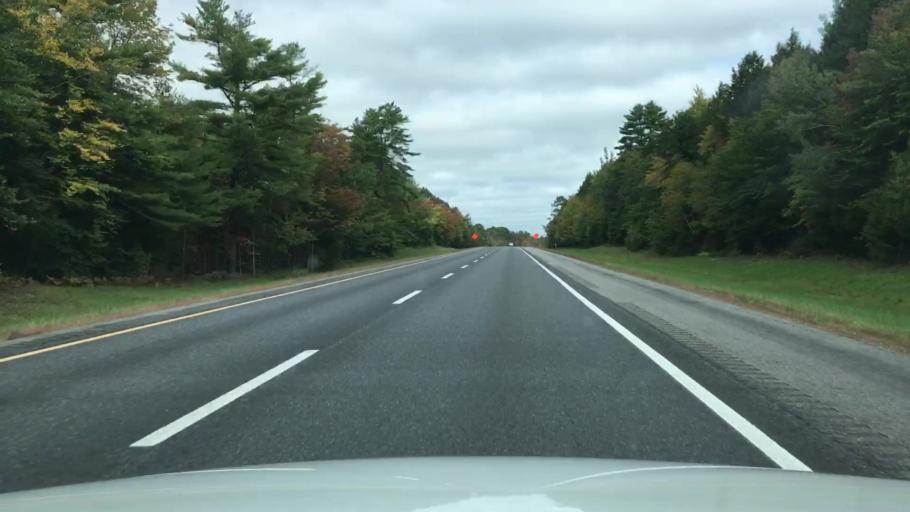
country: US
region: Maine
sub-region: Sagadahoc County
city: Richmond
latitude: 44.0868
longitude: -69.8753
